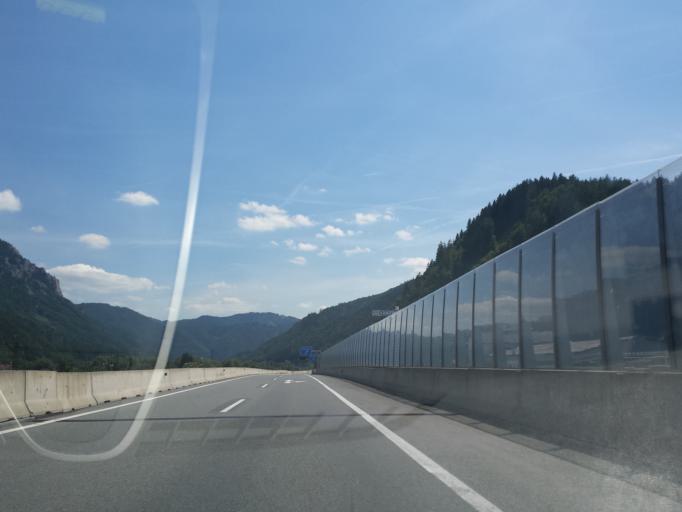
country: AT
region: Styria
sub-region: Politischer Bezirk Bruck-Muerzzuschlag
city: Pernegg an der Mur
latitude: 47.3446
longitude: 15.3479
